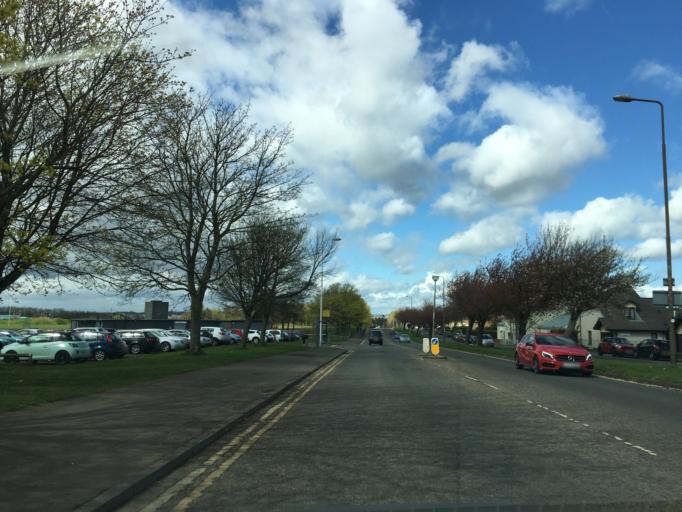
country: GB
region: Scotland
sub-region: Edinburgh
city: Colinton
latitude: 55.9255
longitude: -3.2826
